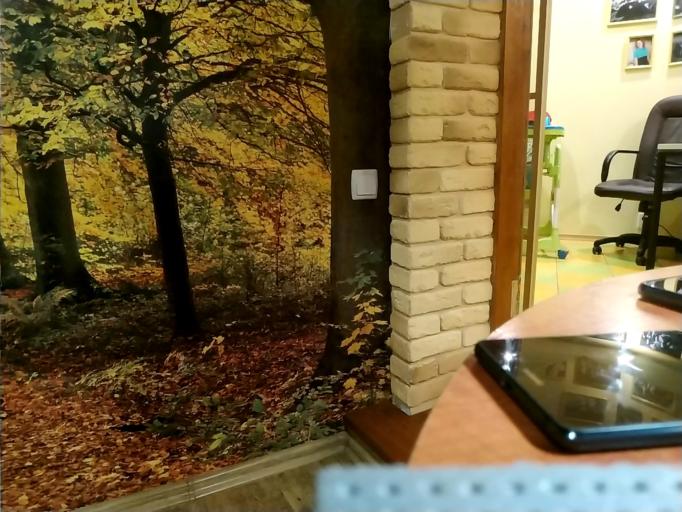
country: RU
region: Tverskaya
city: Zubtsov
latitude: 56.2051
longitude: 34.7158
